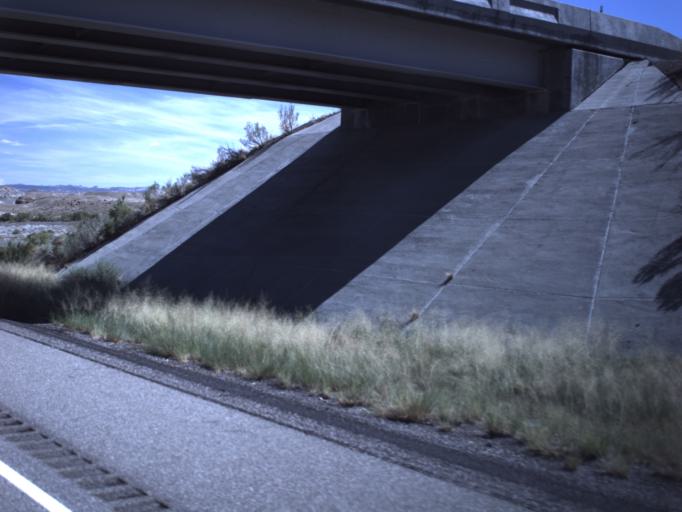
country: US
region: Utah
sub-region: Emery County
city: Ferron
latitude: 38.8111
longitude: -111.2109
